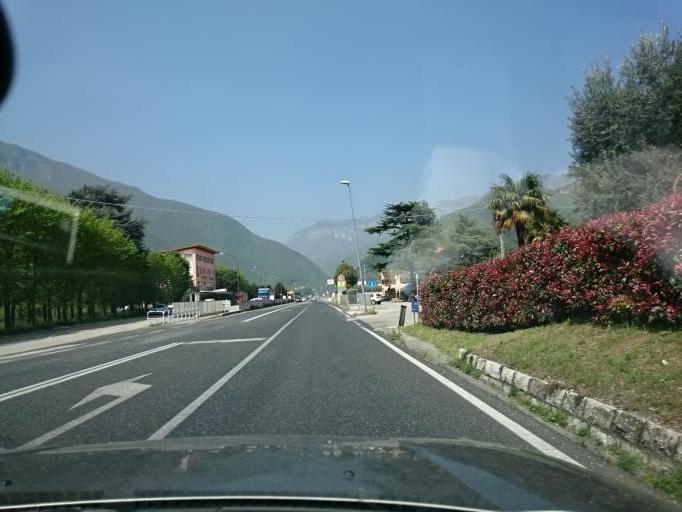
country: IT
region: Veneto
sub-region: Provincia di Vicenza
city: Pove del Grappa
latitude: 45.7939
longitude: 11.7235
